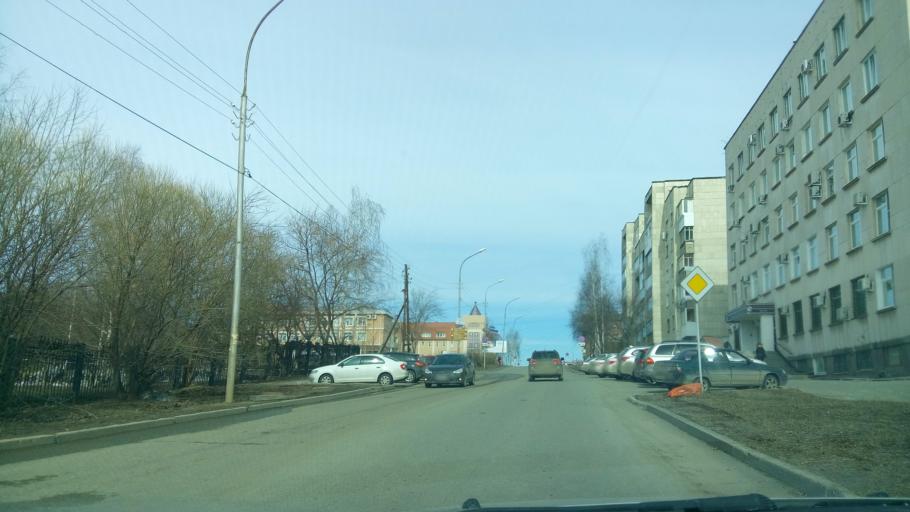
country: RU
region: Sverdlovsk
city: Nizhniy Tagil
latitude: 57.9051
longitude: 59.9610
